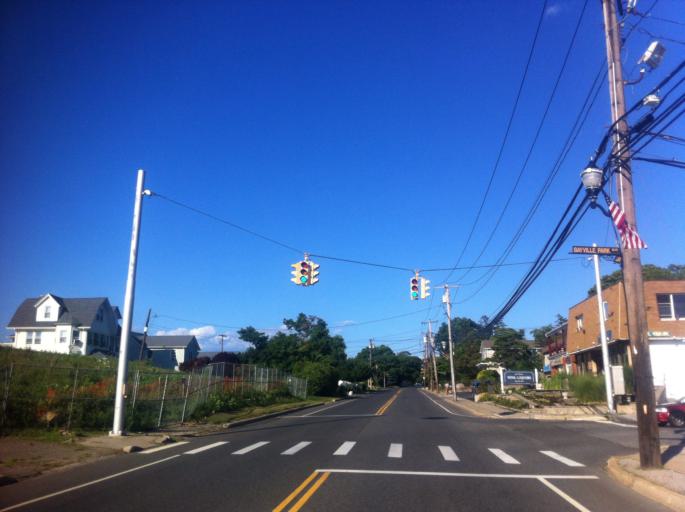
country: US
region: New York
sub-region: Nassau County
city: Bayville
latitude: 40.9090
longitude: -73.5797
